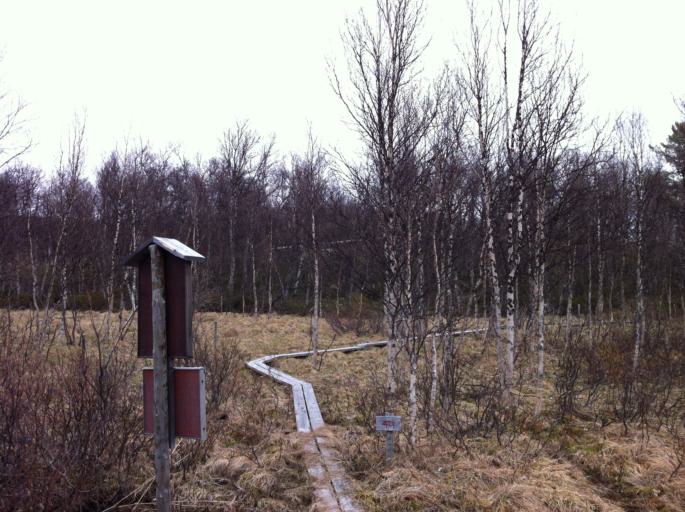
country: NO
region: Sor-Trondelag
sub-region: Tydal
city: Aas
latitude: 62.5538
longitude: 12.3130
